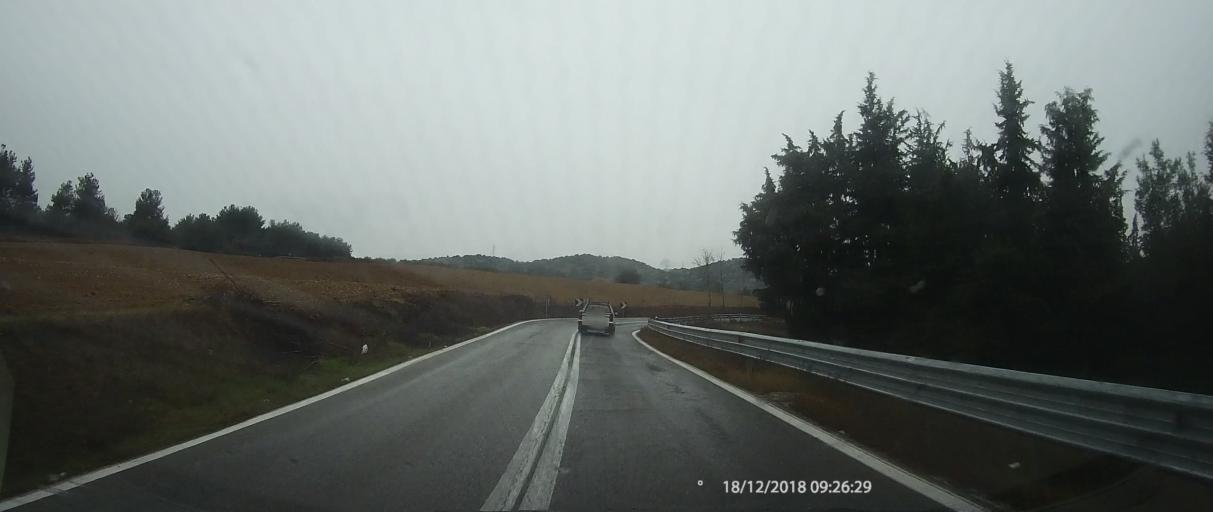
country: GR
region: Thessaly
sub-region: Nomos Larisis
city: Elassona
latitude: 39.9143
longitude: 22.1830
